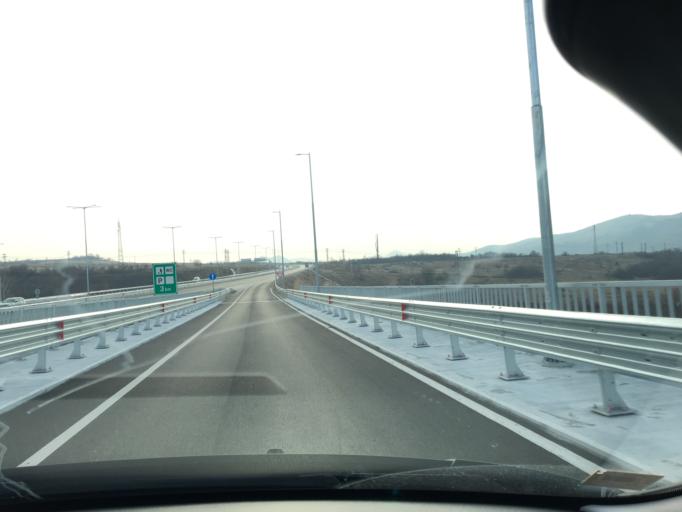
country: BG
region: Blagoevgrad
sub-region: Obshtina Sandanski
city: Sandanski
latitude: 41.5394
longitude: 23.2571
